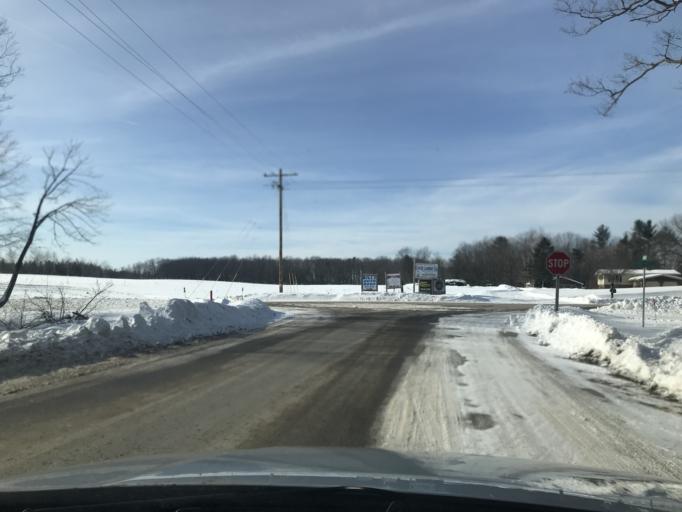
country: US
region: Wisconsin
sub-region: Oconto County
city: Oconto Falls
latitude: 45.1477
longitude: -88.1873
